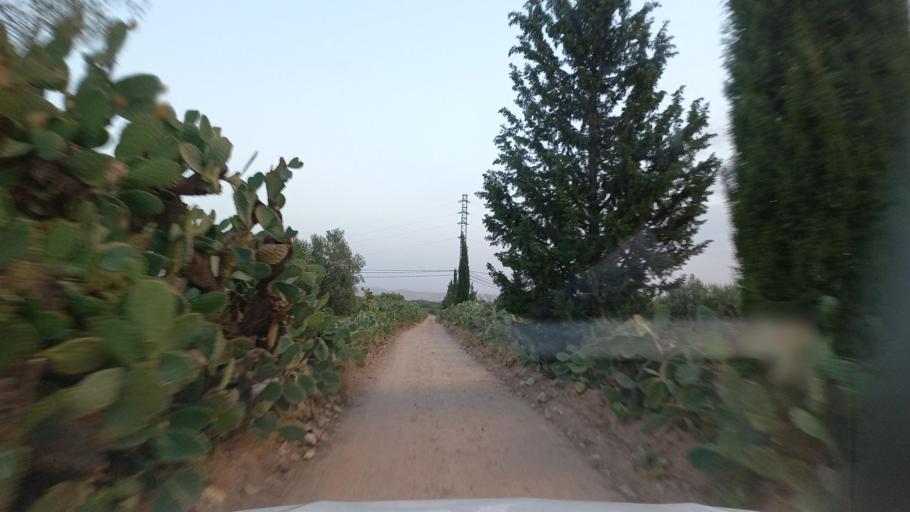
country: TN
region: Al Qasrayn
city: Kasserine
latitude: 35.2754
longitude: 9.0465
